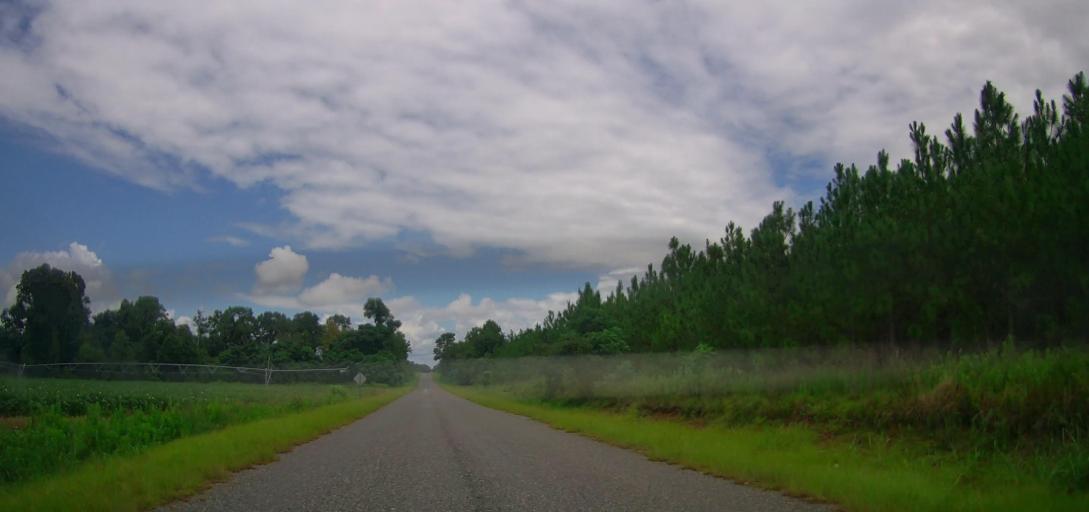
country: US
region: Georgia
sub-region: Dooly County
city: Vienna
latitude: 32.0453
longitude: -83.6277
